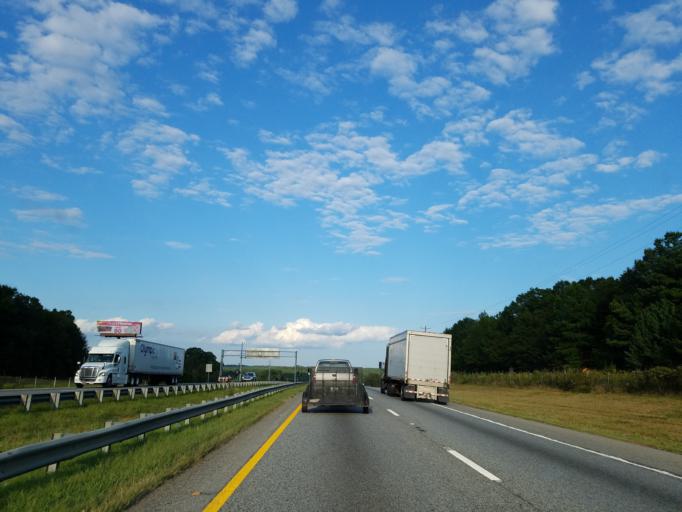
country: US
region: South Carolina
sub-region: Spartanburg County
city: Mayo
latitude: 35.0293
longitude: -81.8647
